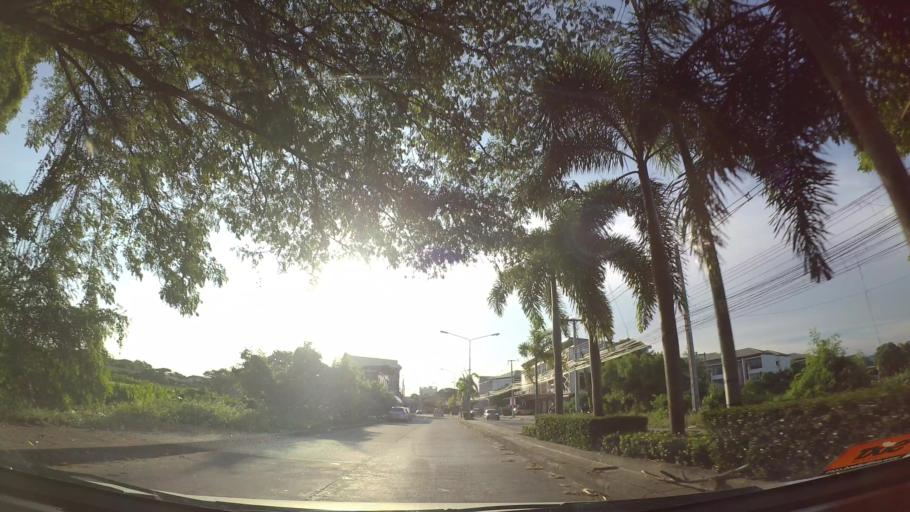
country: TH
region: Rayong
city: Rayong
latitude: 12.6871
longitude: 101.2804
